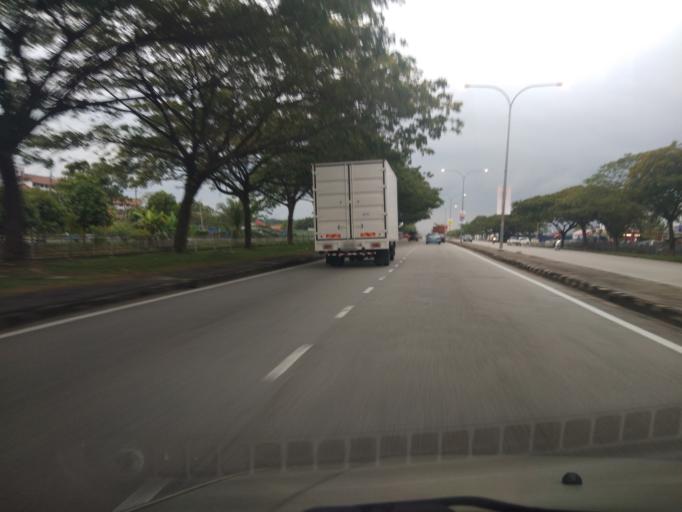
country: MY
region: Penang
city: Kepala Batas
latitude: 5.5181
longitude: 100.4504
